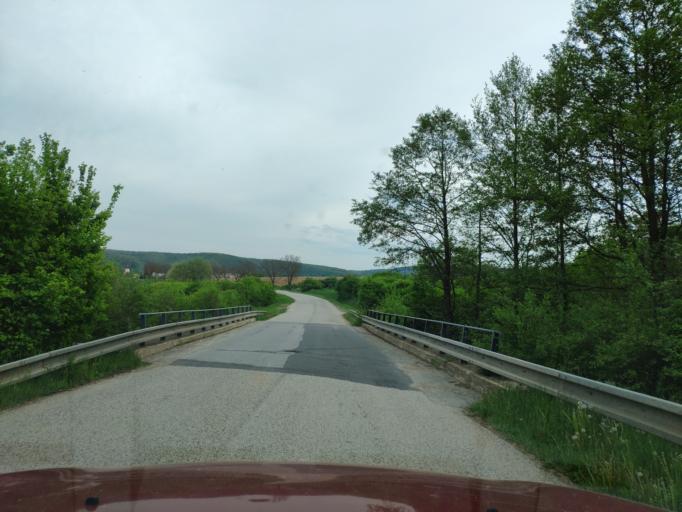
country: SK
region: Banskobystricky
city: Revuca
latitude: 48.4851
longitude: 20.2652
